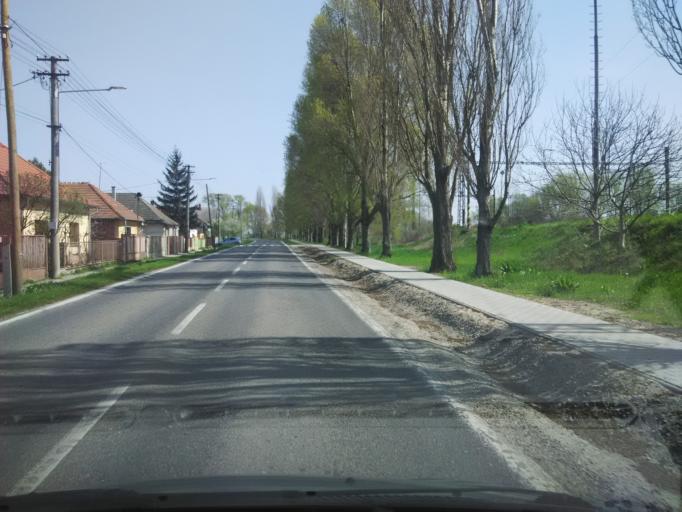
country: SK
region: Nitriansky
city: Sellye
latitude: 48.1517
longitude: 17.9373
